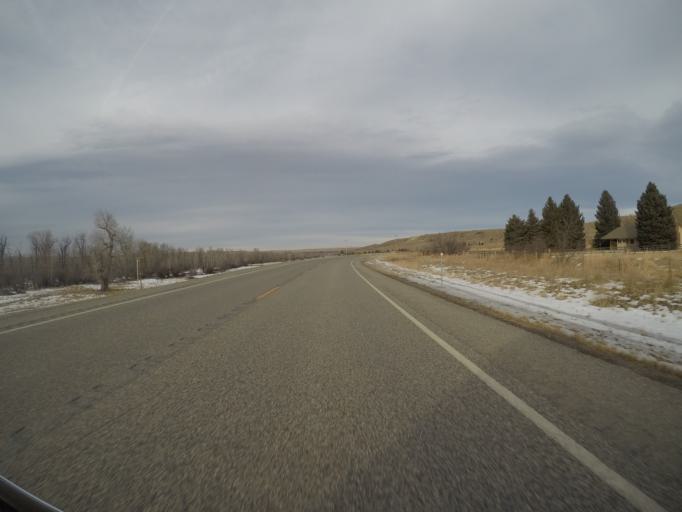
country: US
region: Montana
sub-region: Stillwater County
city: Absarokee
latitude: 45.4707
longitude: -109.4485
